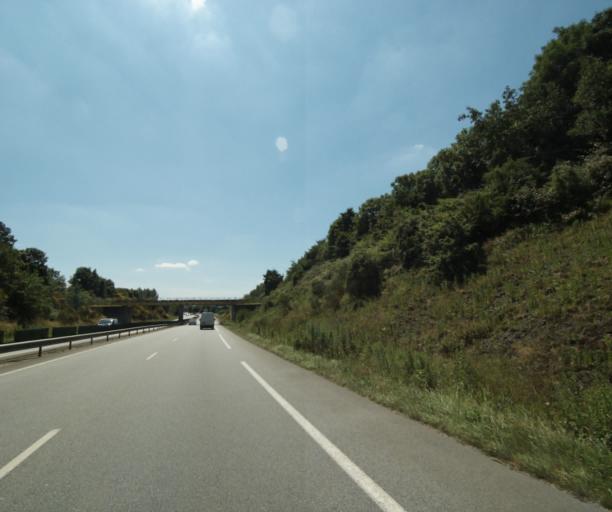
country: FR
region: Pays de la Loire
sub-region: Departement de la Mayenne
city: Bonchamp-les-Laval
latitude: 48.0780
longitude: -0.7295
